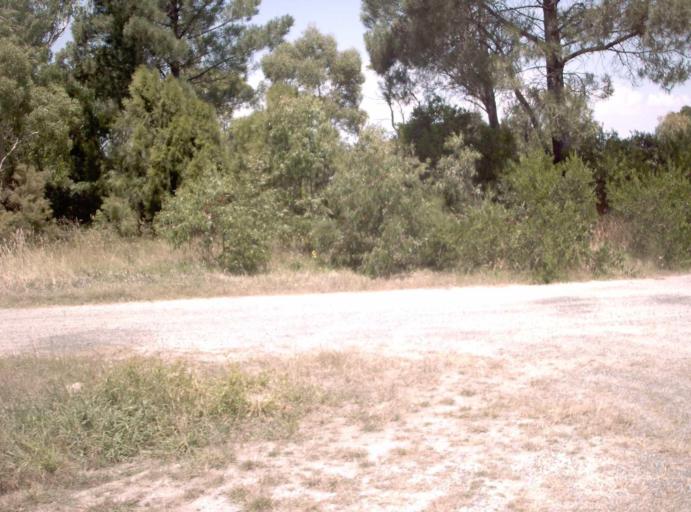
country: AU
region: Victoria
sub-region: Bass Coast
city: North Wonthaggi
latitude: -38.6839
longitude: 145.8836
